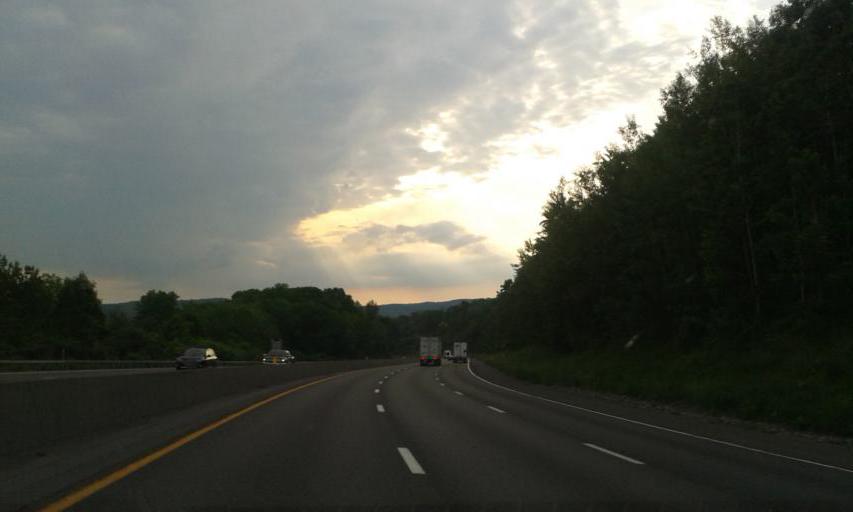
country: US
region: New York
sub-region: Broome County
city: Port Dickinson
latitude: 42.1103
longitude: -75.8694
